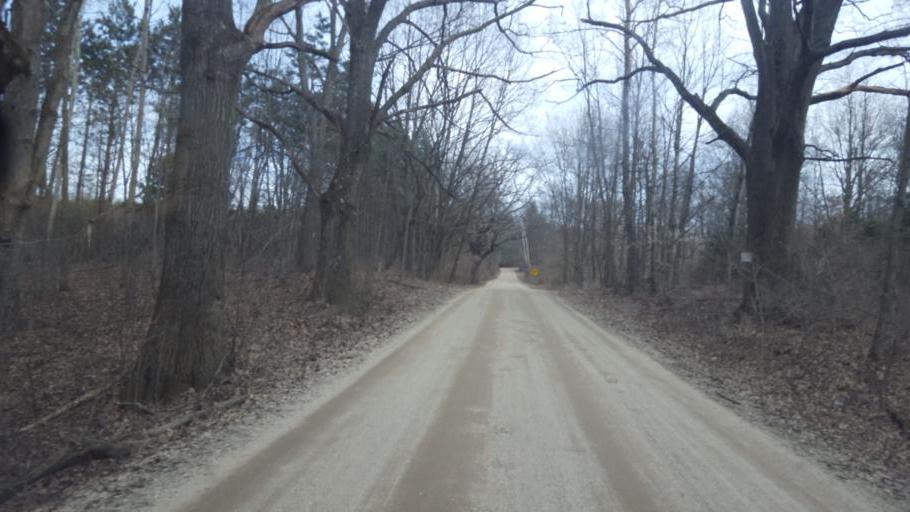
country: US
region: Michigan
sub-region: Isabella County
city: Lake Isabella
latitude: 43.6829
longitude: -85.1406
